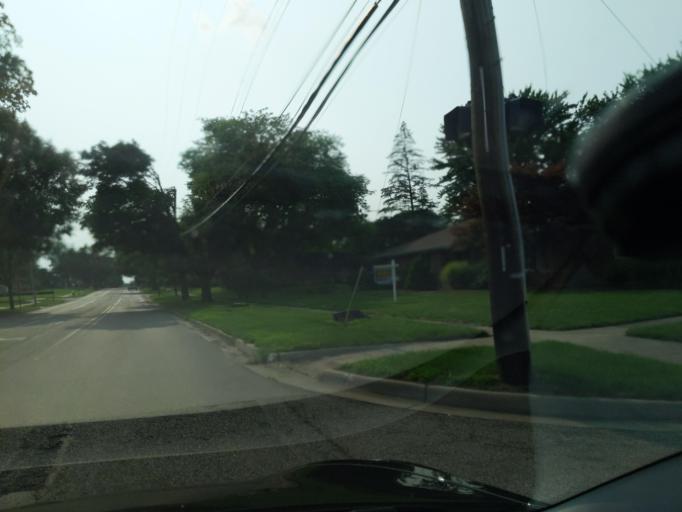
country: US
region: Michigan
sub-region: Jackson County
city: Jackson
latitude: 42.2401
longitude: -84.4283
